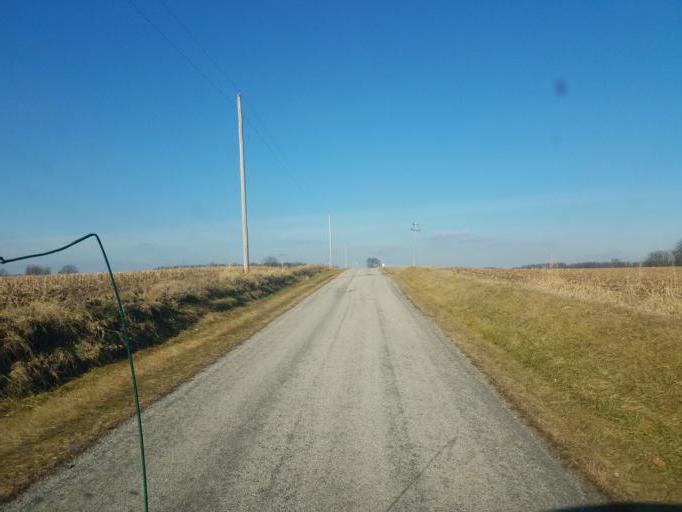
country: US
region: Ohio
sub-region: Wyandot County
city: Upper Sandusky
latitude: 40.6719
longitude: -83.3623
